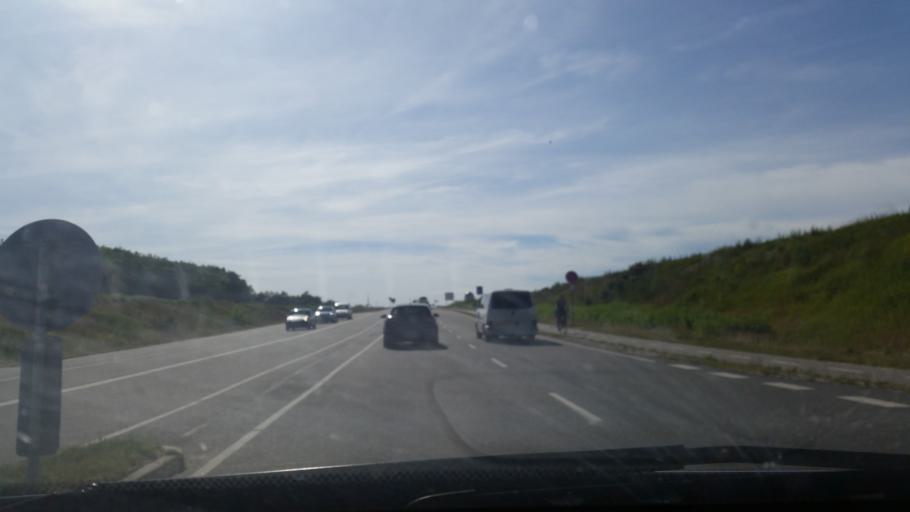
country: DK
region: Central Jutland
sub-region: Samso Kommune
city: Tranebjerg
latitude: 55.8078
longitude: 10.6433
